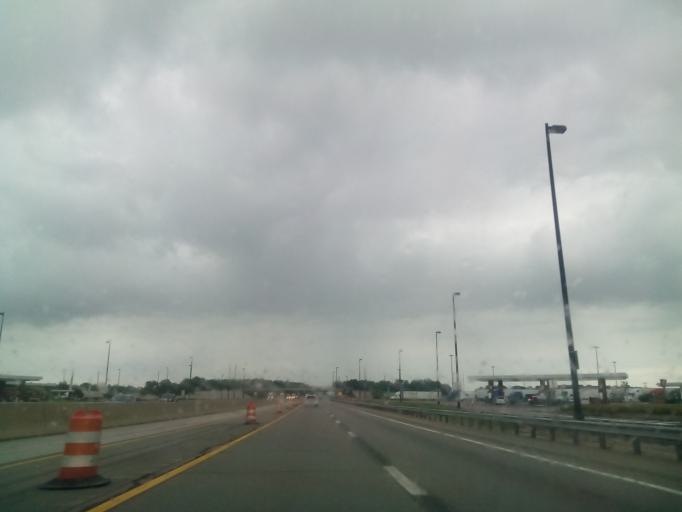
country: US
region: Ohio
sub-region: Sandusky County
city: Clyde
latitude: 41.3688
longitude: -82.9593
